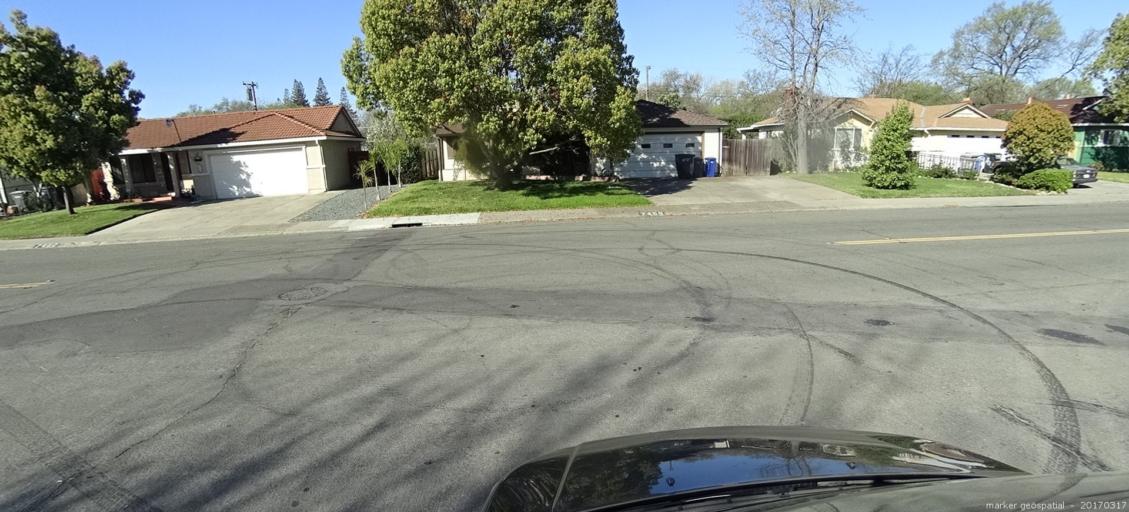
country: US
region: California
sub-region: Sacramento County
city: Parkway
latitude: 38.4869
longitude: -121.5049
